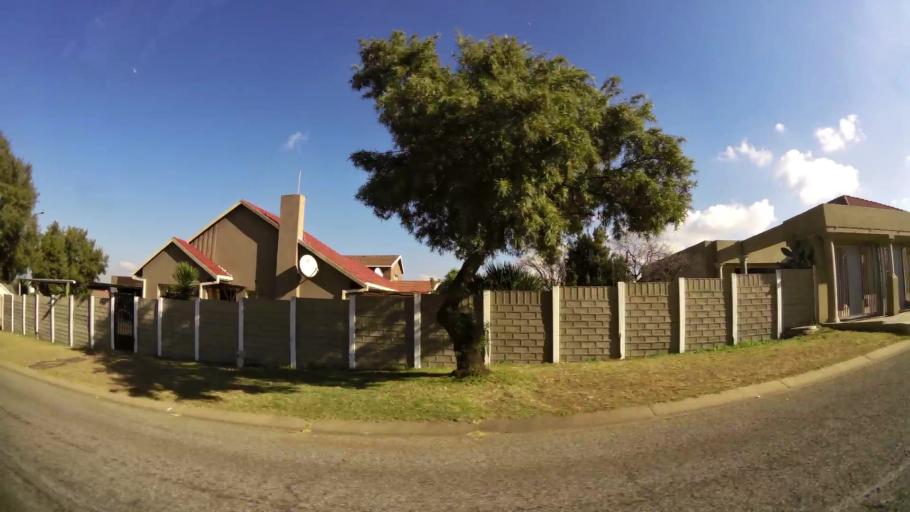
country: ZA
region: Gauteng
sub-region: City of Johannesburg Metropolitan Municipality
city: Roodepoort
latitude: -26.1642
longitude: 27.8178
